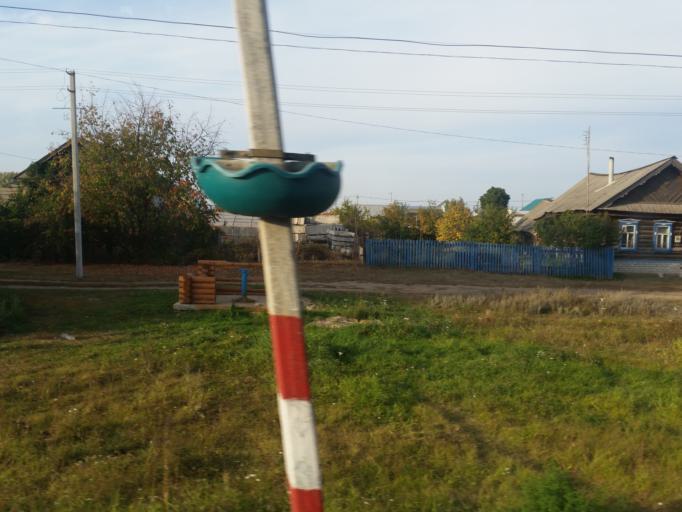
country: RU
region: Ulyanovsk
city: Cherdakly
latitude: 54.3554
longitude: 48.8711
